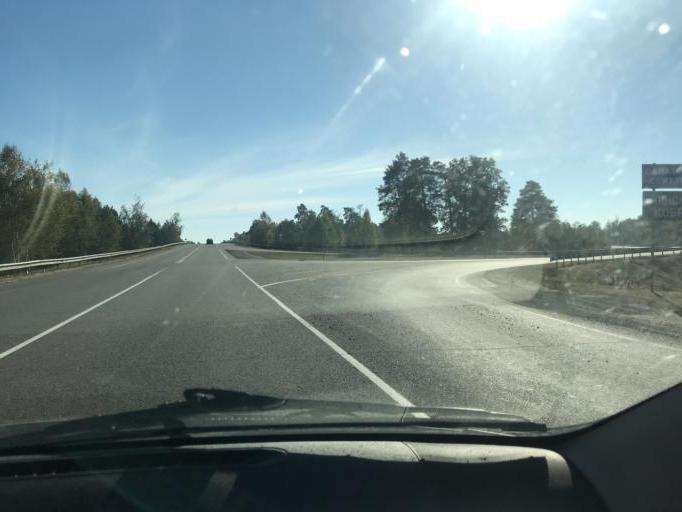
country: BY
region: Brest
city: Mikashevichy
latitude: 52.2466
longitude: 27.4428
